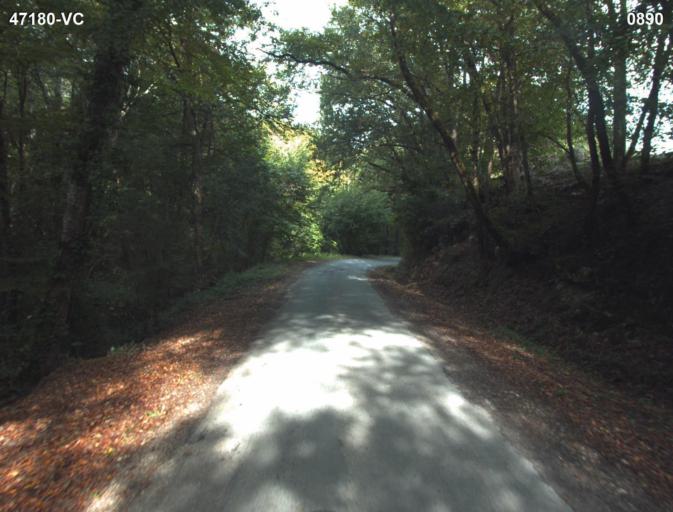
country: FR
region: Aquitaine
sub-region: Departement du Lot-et-Garonne
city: Sainte-Colombe-en-Bruilhois
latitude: 44.1820
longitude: 0.4389
